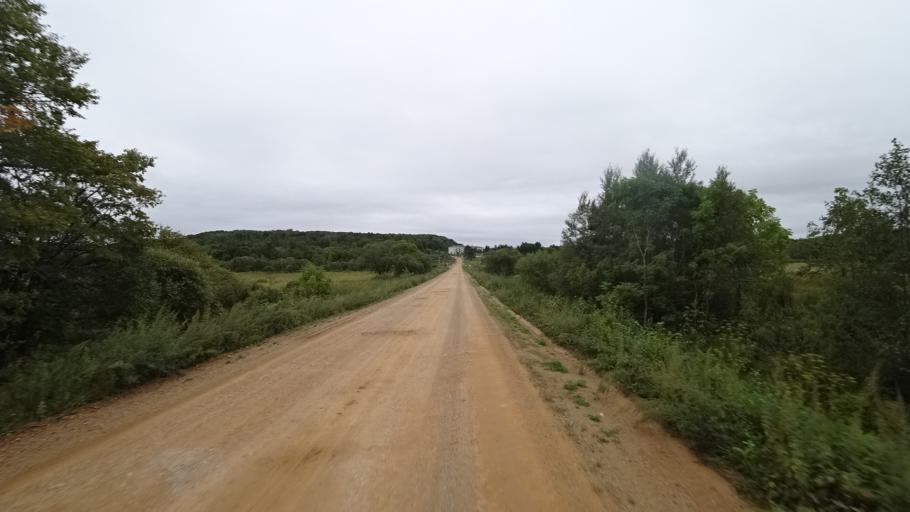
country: RU
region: Primorskiy
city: Rettikhovka
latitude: 44.1762
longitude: 132.8768
